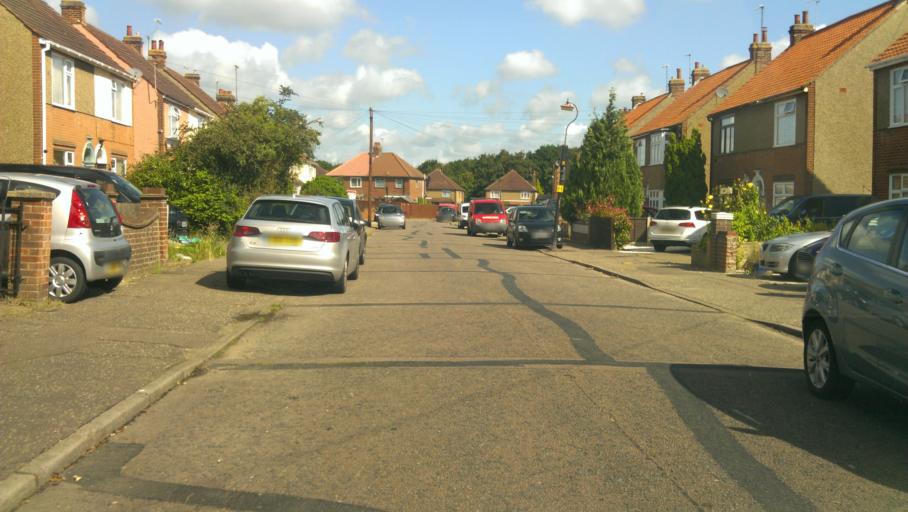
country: GB
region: England
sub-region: Essex
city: Colchester
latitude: 51.8740
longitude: 0.9197
